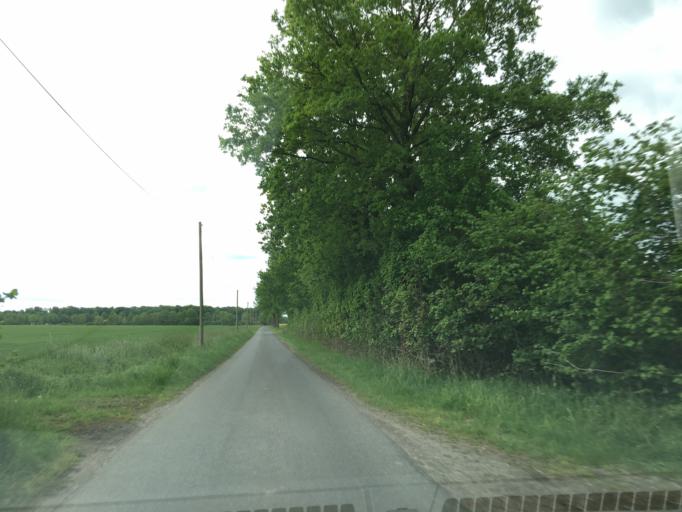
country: DE
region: North Rhine-Westphalia
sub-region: Regierungsbezirk Munster
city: Senden
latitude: 51.9000
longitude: 7.5659
